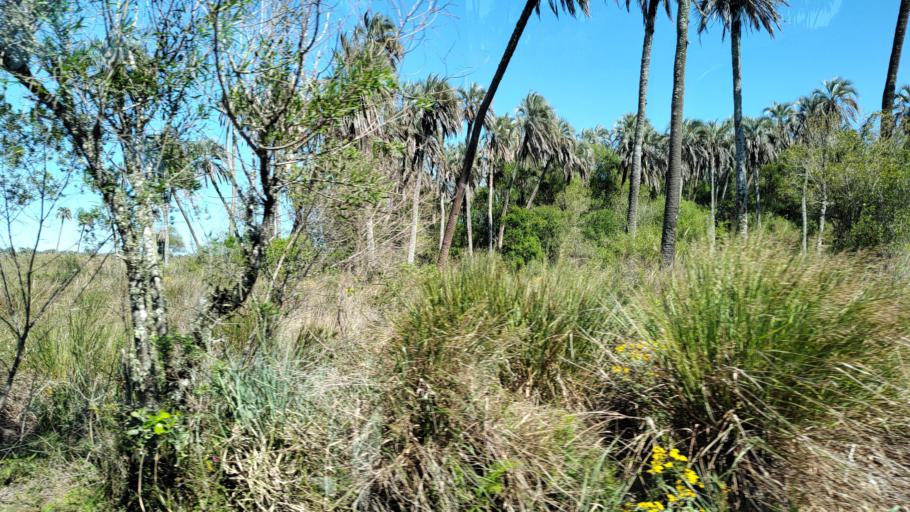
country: AR
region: Entre Rios
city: Ubajay
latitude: -31.8820
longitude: -58.2365
